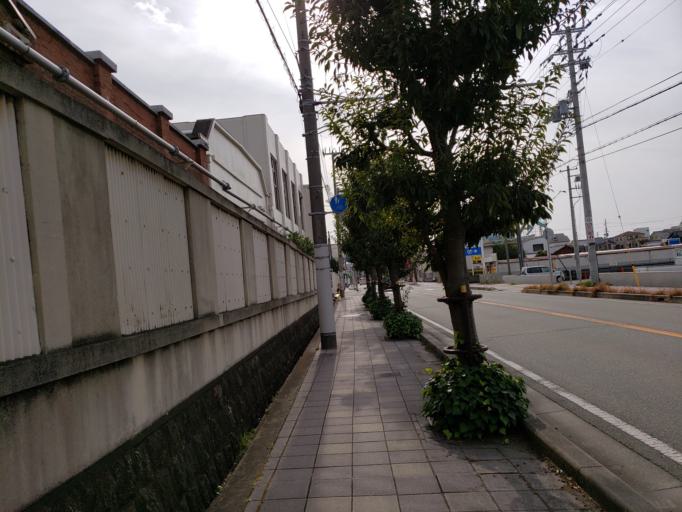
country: JP
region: Hyogo
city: Kakogawacho-honmachi
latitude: 34.7499
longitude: 134.8039
